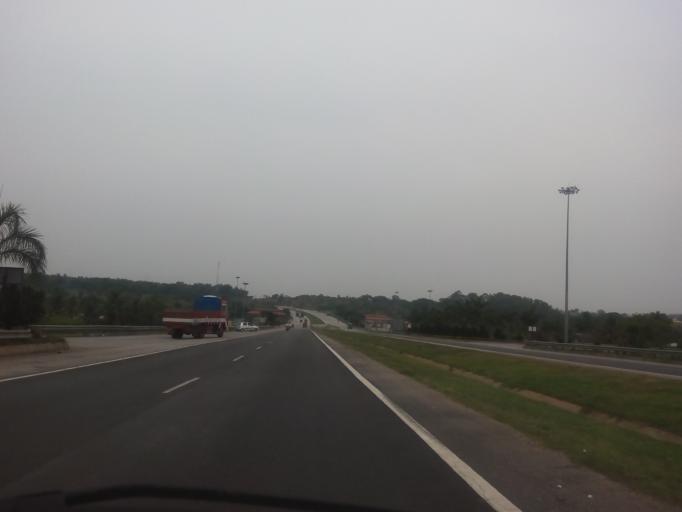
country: IN
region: Karnataka
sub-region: Bangalore Urban
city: Bangalore
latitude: 12.9059
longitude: 77.4693
